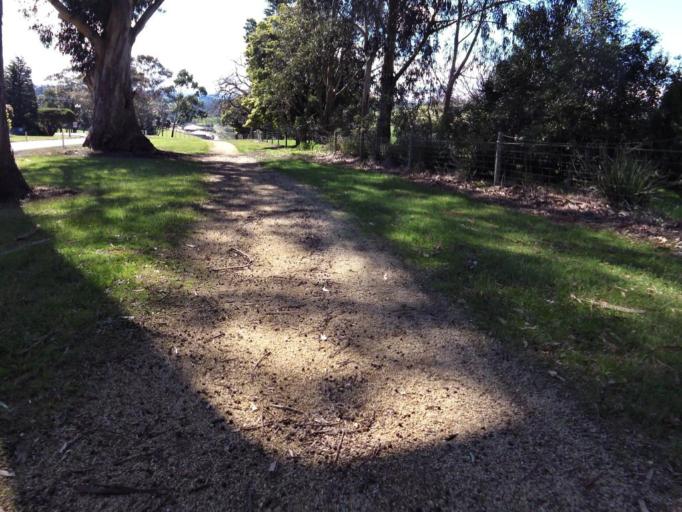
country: AU
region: Victoria
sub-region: Baw Baw
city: Warragul
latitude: -38.0296
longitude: 145.9553
